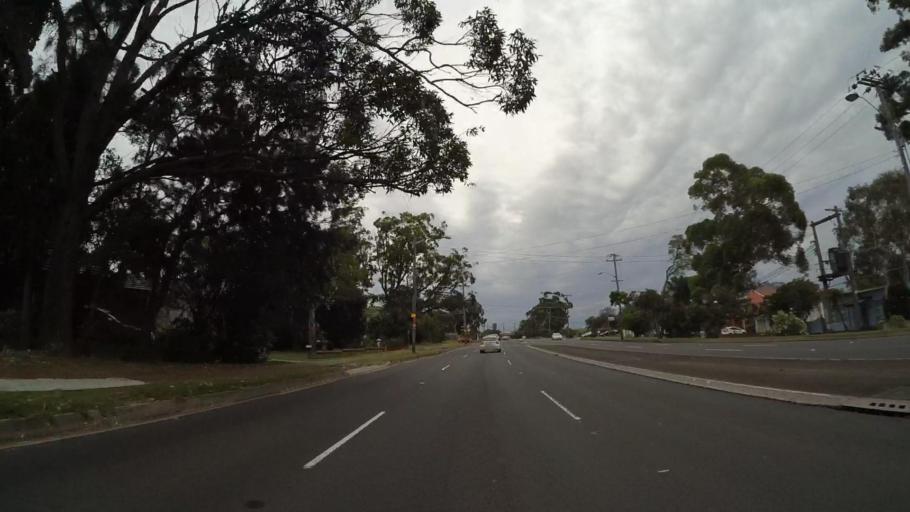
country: AU
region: New South Wales
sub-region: Sutherland Shire
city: Kareela
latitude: -34.0166
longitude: 151.0928
